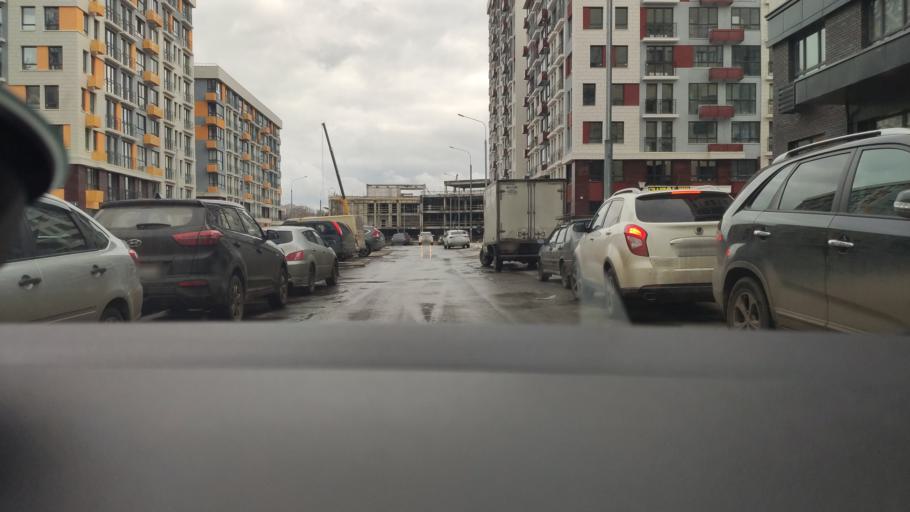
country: RU
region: Moskovskaya
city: Mosrentgen
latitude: 55.5930
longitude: 37.4598
